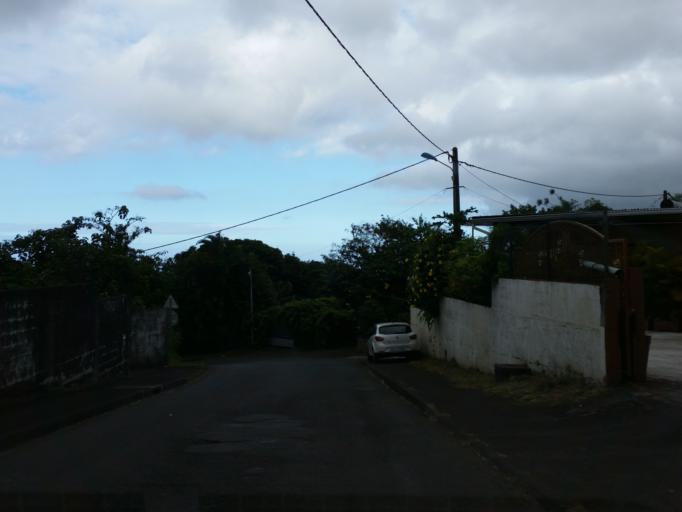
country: RE
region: Reunion
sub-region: Reunion
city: Sainte-Marie
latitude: -20.9312
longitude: 55.5411
